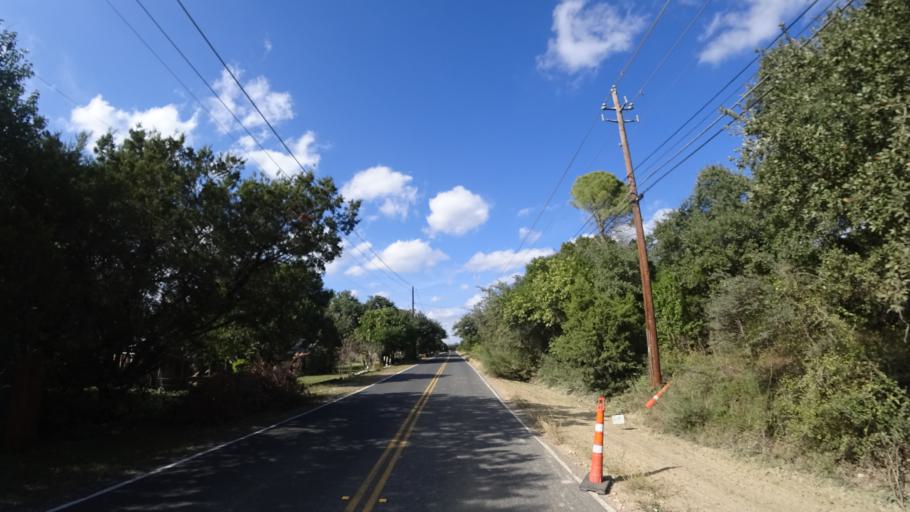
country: US
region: Texas
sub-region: Travis County
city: Barton Creek
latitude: 30.2411
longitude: -97.8774
